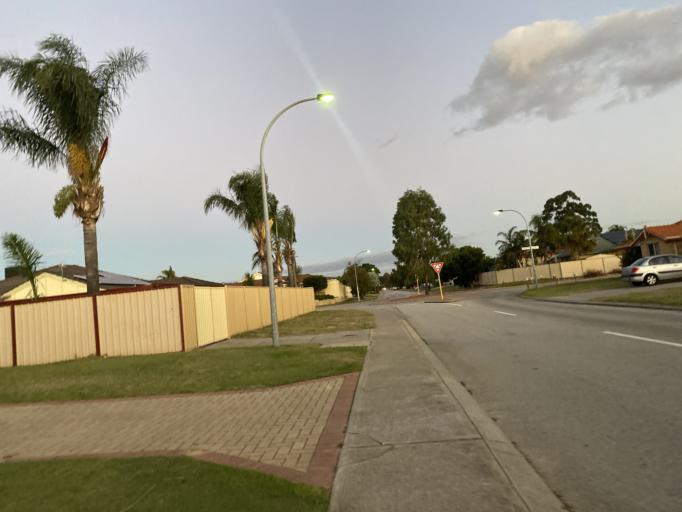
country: AU
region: Western Australia
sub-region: Belmont
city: Kewdale
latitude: -31.9881
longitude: 115.9897
